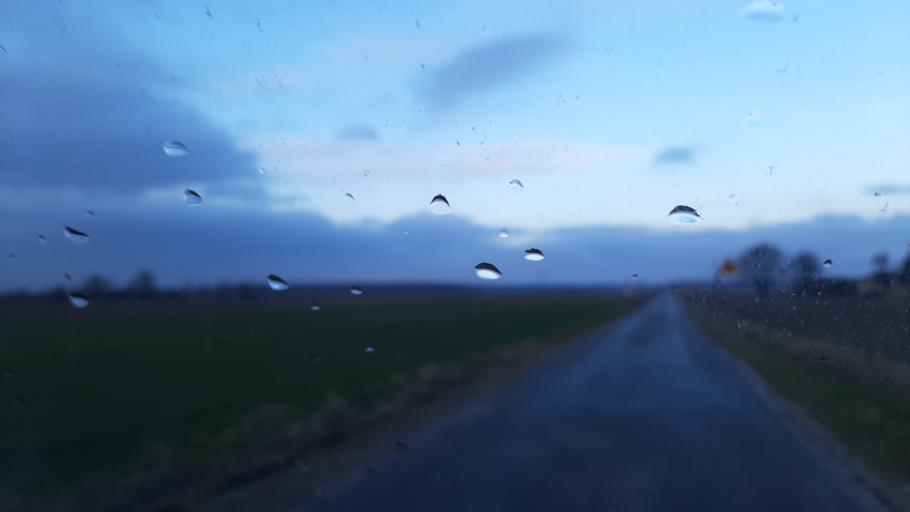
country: PL
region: Lublin Voivodeship
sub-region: Powiat lubelski
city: Jastkow
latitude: 51.3565
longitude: 22.3953
